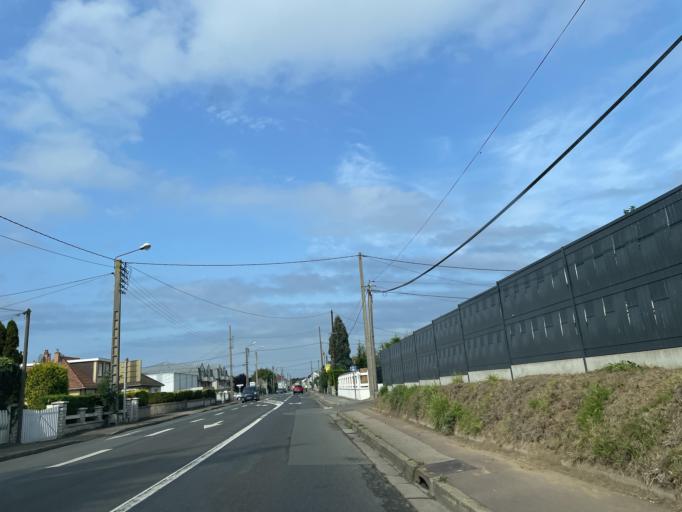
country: FR
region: Picardie
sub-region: Departement de la Somme
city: Mers-les-Bains
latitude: 50.0615
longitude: 1.4062
